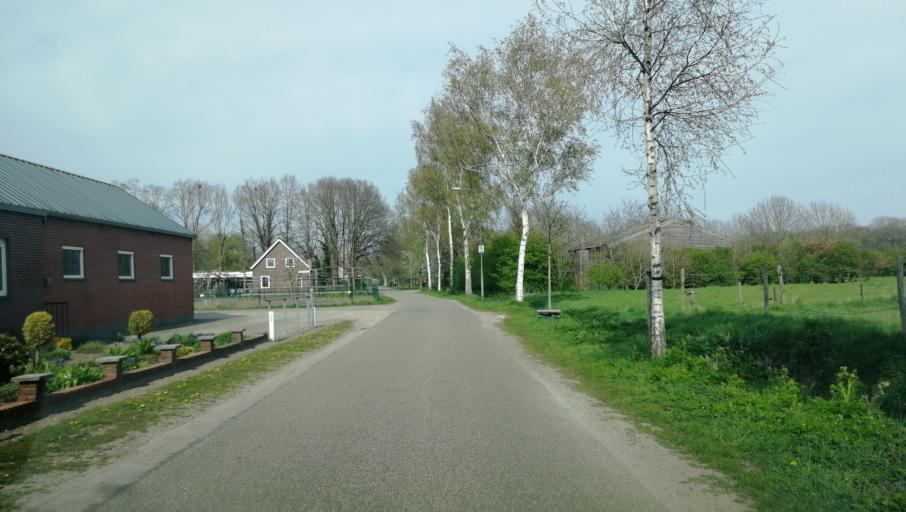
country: NL
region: Limburg
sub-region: Gemeente Peel en Maas
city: Maasbree
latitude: 51.3664
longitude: 6.0803
